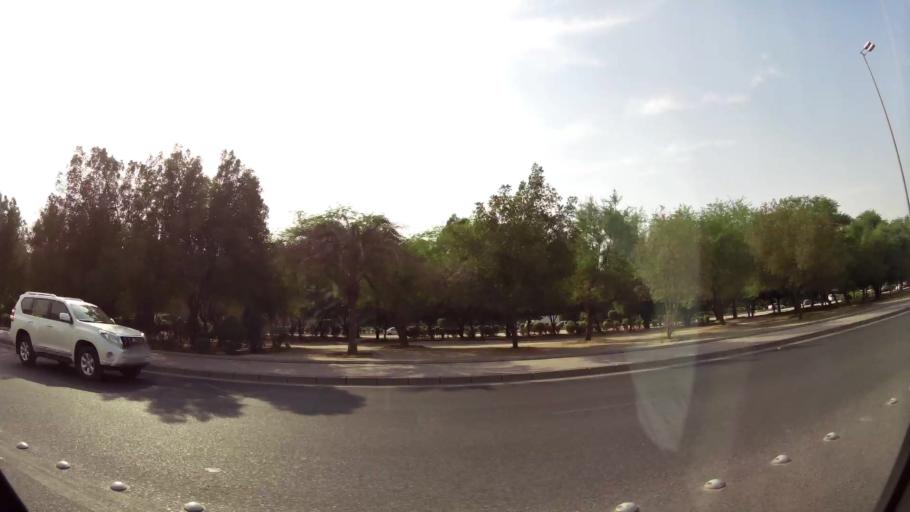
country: KW
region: Al Farwaniyah
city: Al Farwaniyah
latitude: 29.2850
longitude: 47.9678
